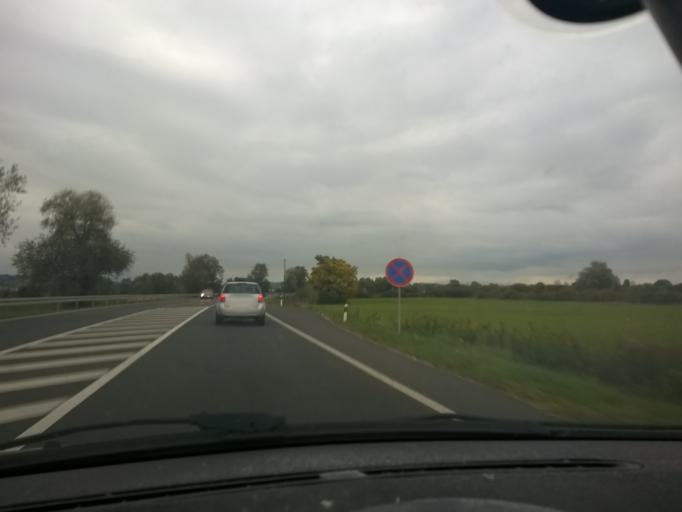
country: HR
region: Zagrebacka
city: Jakovlje
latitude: 45.9855
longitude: 15.8463
